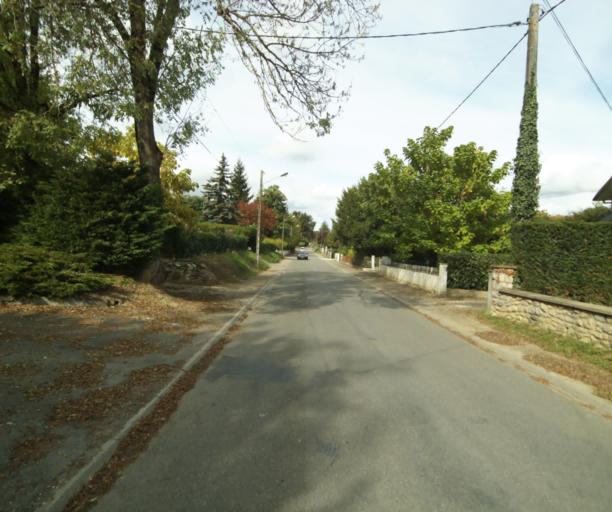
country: FR
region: Midi-Pyrenees
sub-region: Departement du Gers
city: Eauze
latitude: 43.8544
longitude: 0.1030
